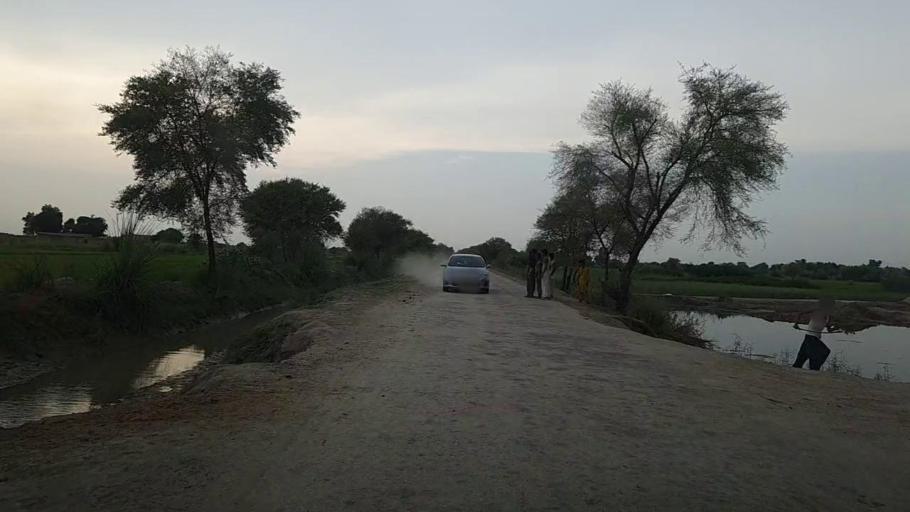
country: PK
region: Sindh
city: Khanpur
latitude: 27.8446
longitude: 69.4608
